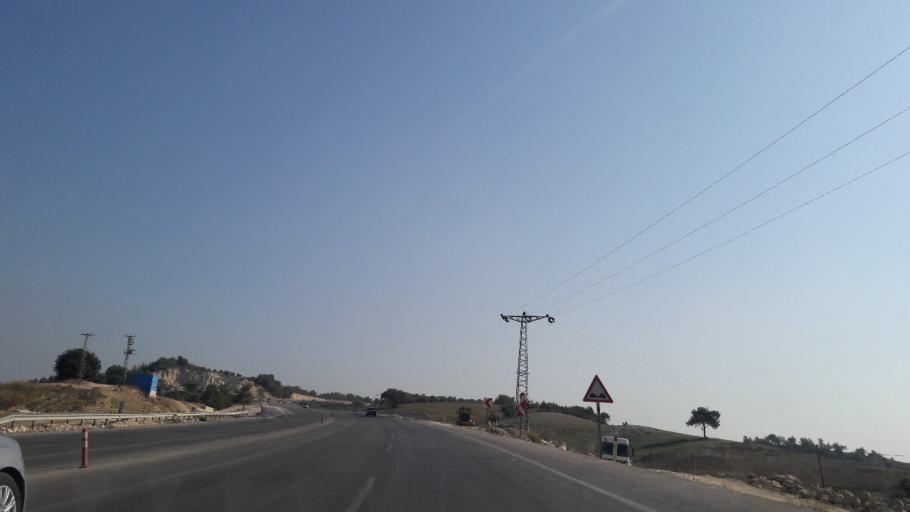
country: TR
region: Adana
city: Yuregir
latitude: 37.0756
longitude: 35.4695
